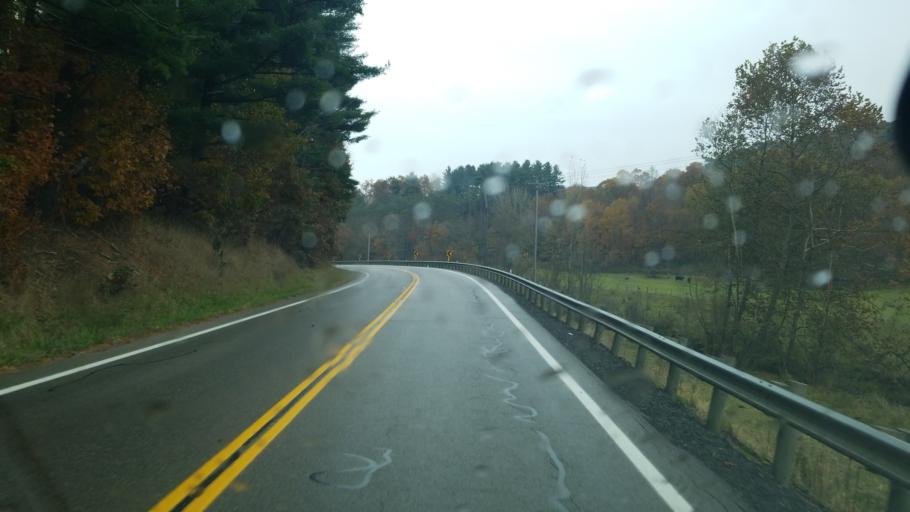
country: US
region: Ohio
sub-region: Coshocton County
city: Coshocton
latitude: 40.3682
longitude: -81.8739
